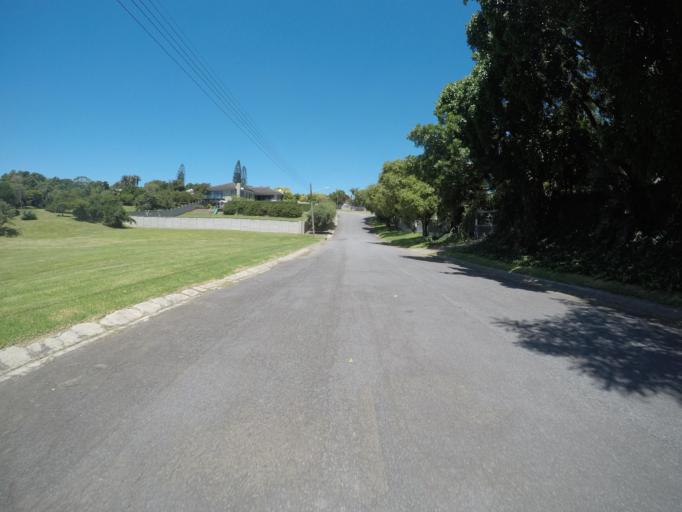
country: ZA
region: Eastern Cape
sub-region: Buffalo City Metropolitan Municipality
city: East London
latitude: -32.9643
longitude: 27.9466
